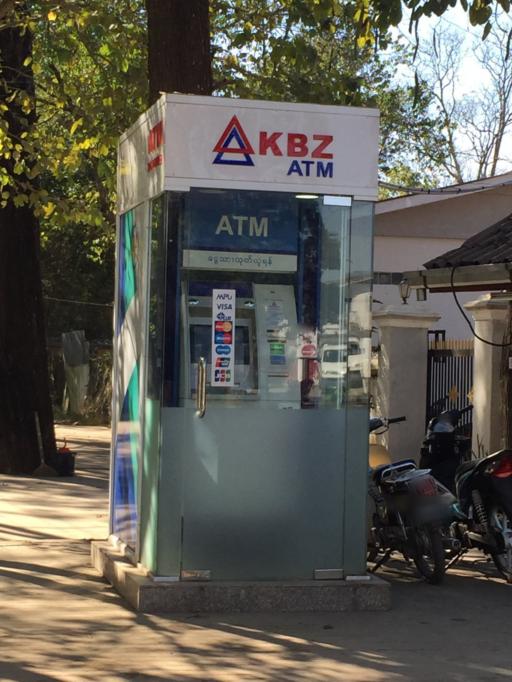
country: MM
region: Mandalay
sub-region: Pyin Oo Lwin District
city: Pyin Oo Lwin
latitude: 22.0150
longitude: 96.4627
